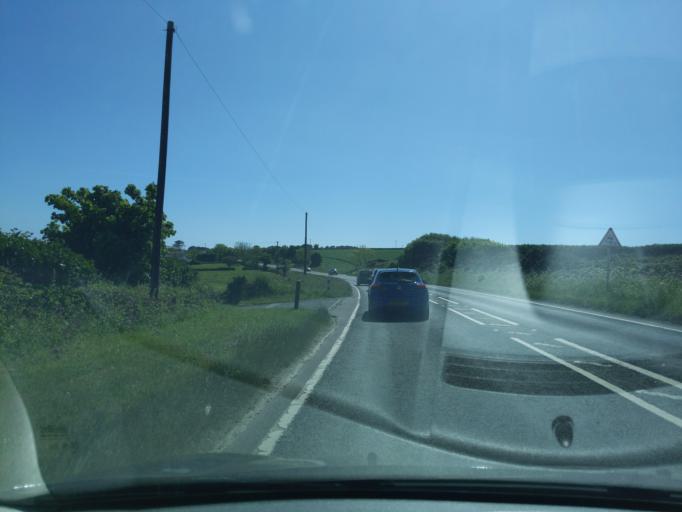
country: GB
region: England
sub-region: Cornwall
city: Wendron
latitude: 50.1487
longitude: -5.2097
